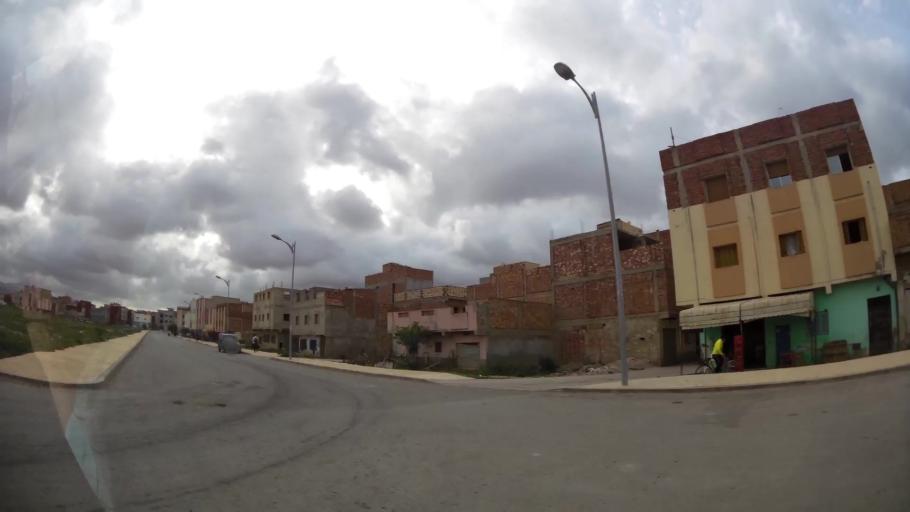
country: MA
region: Oriental
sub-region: Nador
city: Nador
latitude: 35.1584
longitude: -2.9084
